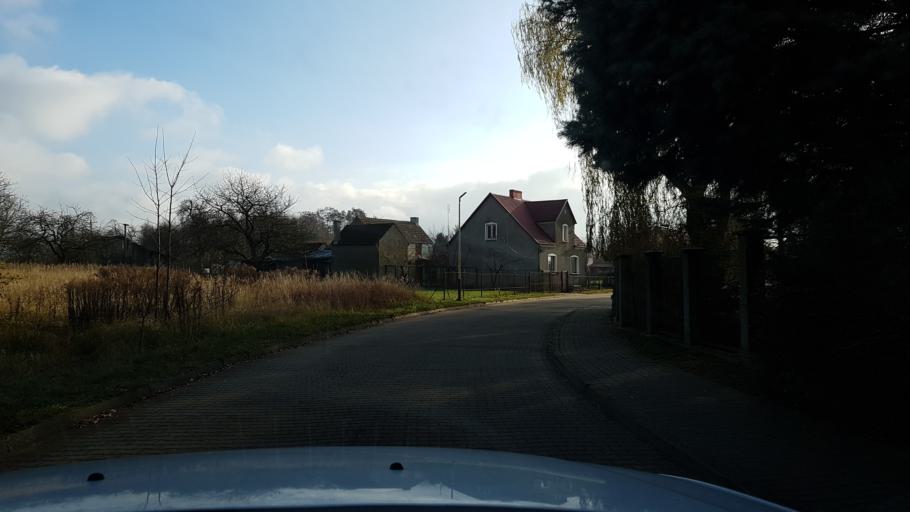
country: PL
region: West Pomeranian Voivodeship
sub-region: Powiat stargardzki
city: Insko
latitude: 53.4345
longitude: 15.5444
